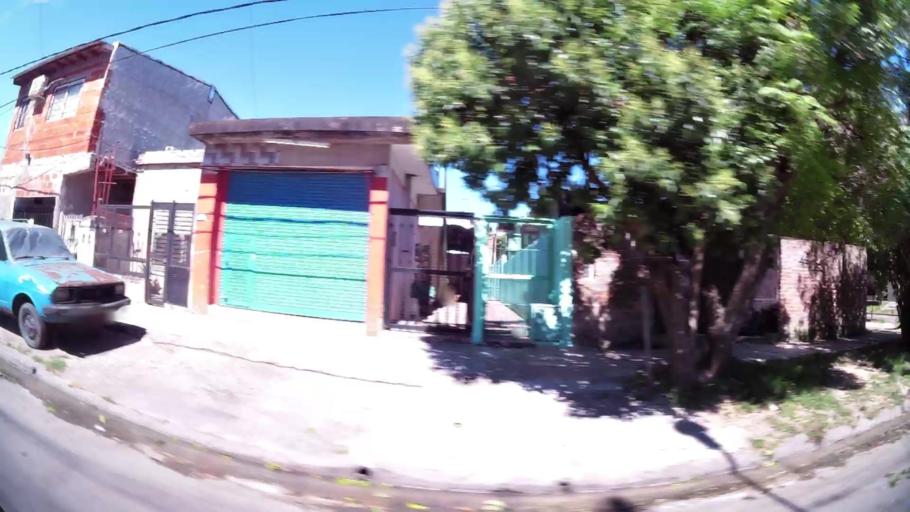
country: AR
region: Buenos Aires
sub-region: Partido de Tigre
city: Tigre
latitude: -34.4999
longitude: -58.6100
